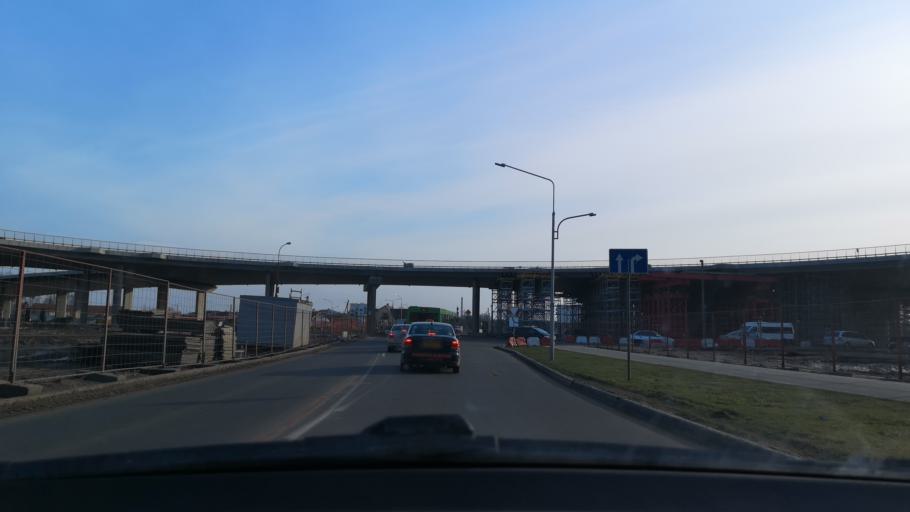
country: BY
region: Brest
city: Brest
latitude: 52.1055
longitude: 23.6654
